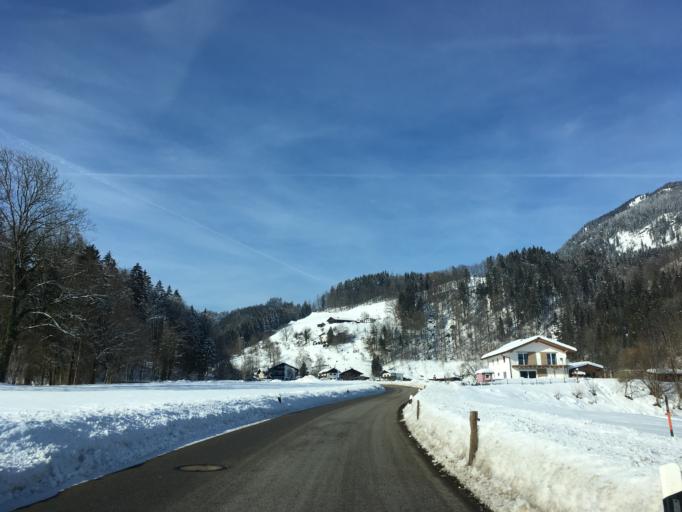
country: DE
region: Bavaria
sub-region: Upper Bavaria
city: Oberaudorf
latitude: 47.6602
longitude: 12.1628
